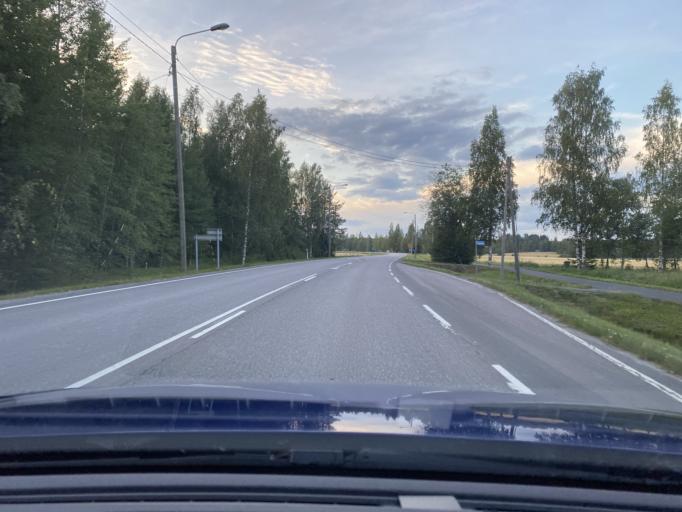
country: FI
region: Satakunta
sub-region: Pohjois-Satakunta
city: Kankaanpaeae
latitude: 61.7567
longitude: 22.5050
